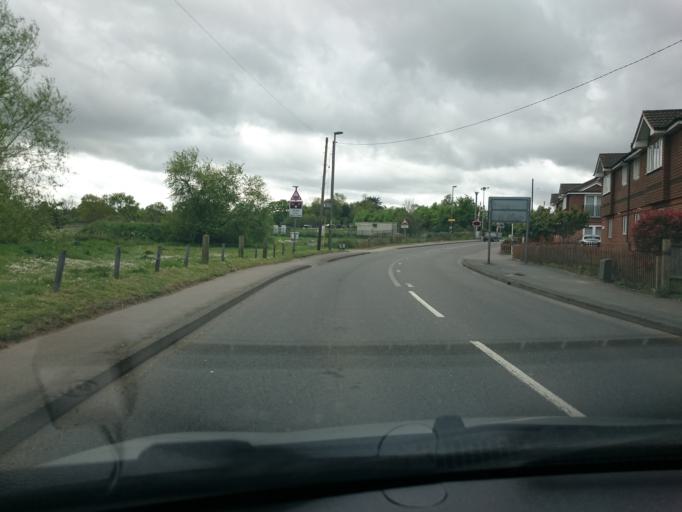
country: GB
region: England
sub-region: Surrey
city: Seale
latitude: 51.2501
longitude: -0.7115
